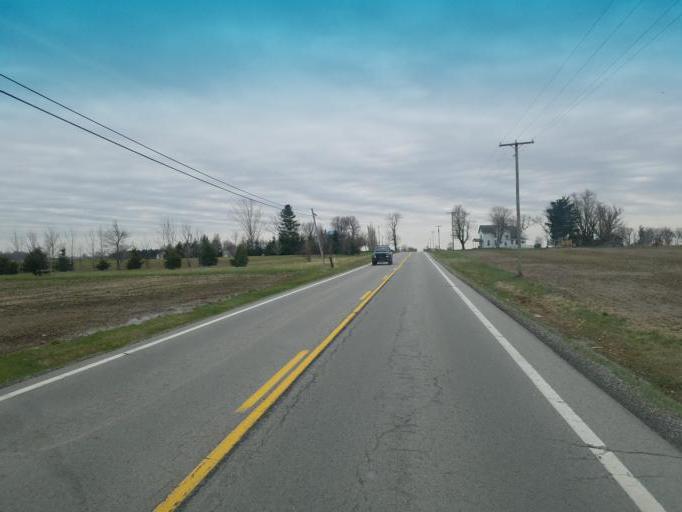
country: US
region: Ohio
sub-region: Crawford County
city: Bucyrus
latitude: 40.8892
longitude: -82.9590
